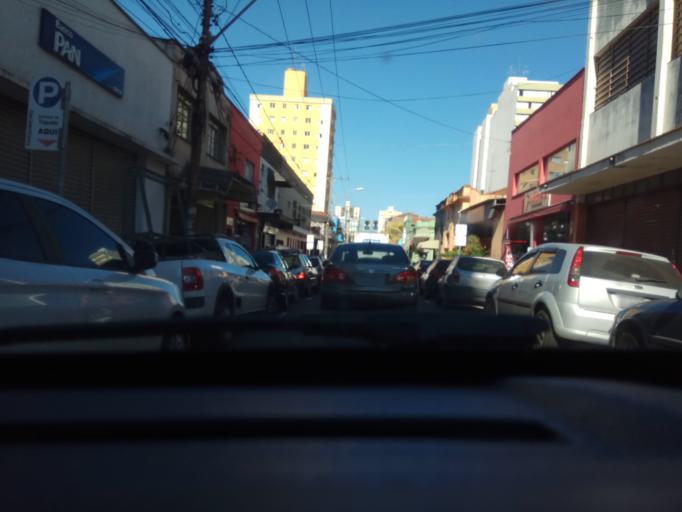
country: BR
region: Sao Paulo
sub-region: Piracicaba
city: Piracicaba
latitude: -22.7257
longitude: -47.6469
